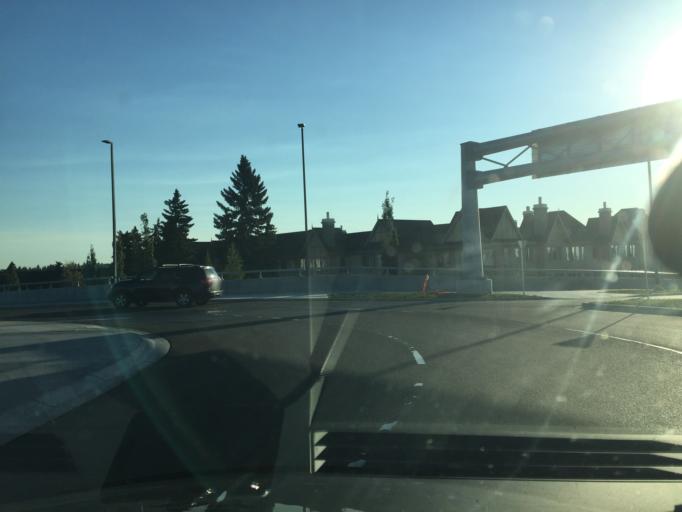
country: CA
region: Alberta
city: Calgary
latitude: 51.0159
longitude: -114.1175
